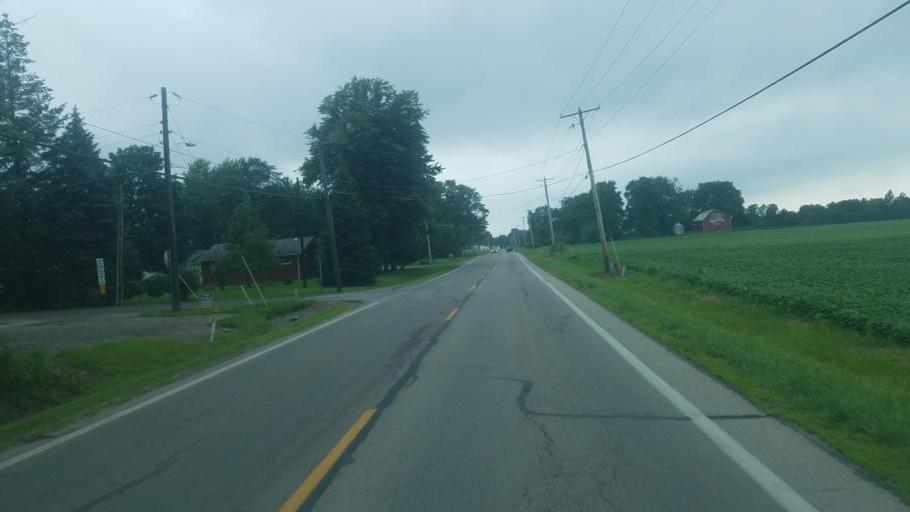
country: US
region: Ohio
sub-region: Logan County
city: Russells Point
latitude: 40.5235
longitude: -83.8731
